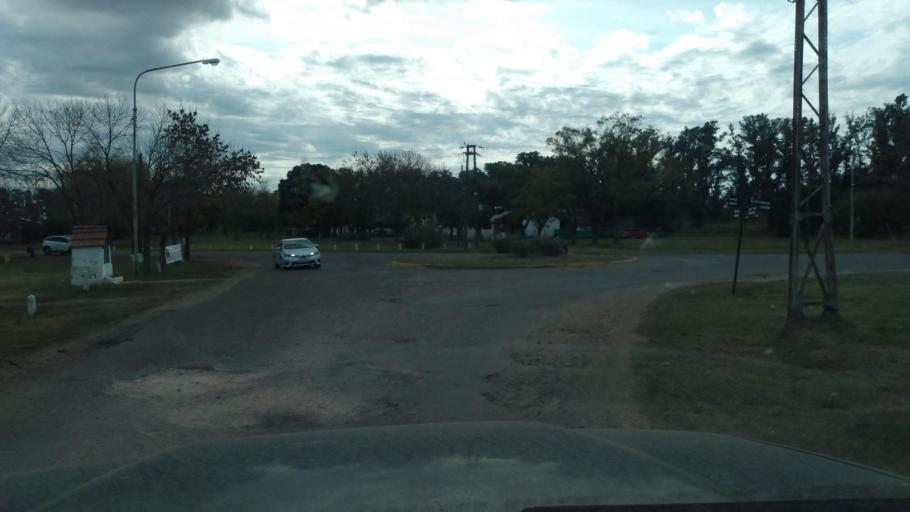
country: AR
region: Buenos Aires
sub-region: Partido de Lujan
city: Lujan
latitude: -34.5997
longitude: -59.1705
